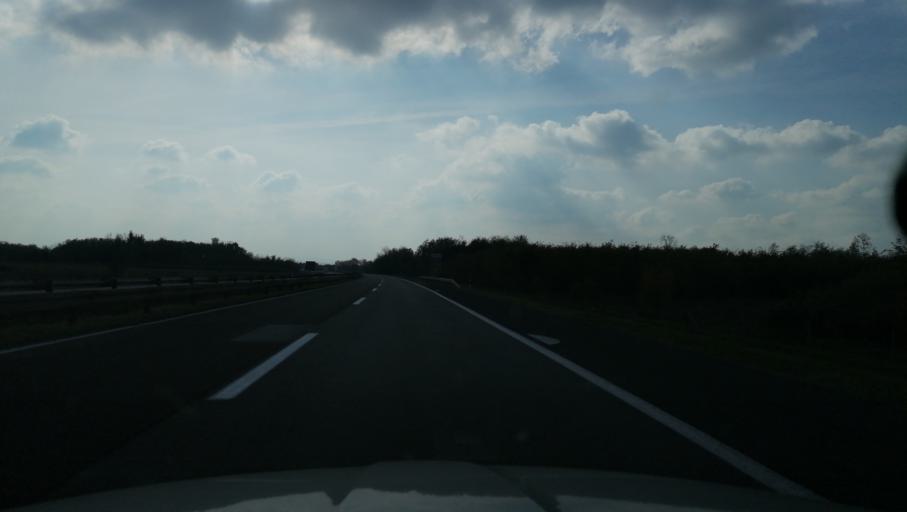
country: RS
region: Central Serbia
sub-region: Sumadijski Okrug
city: Lapovo
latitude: 44.2198
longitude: 21.1091
